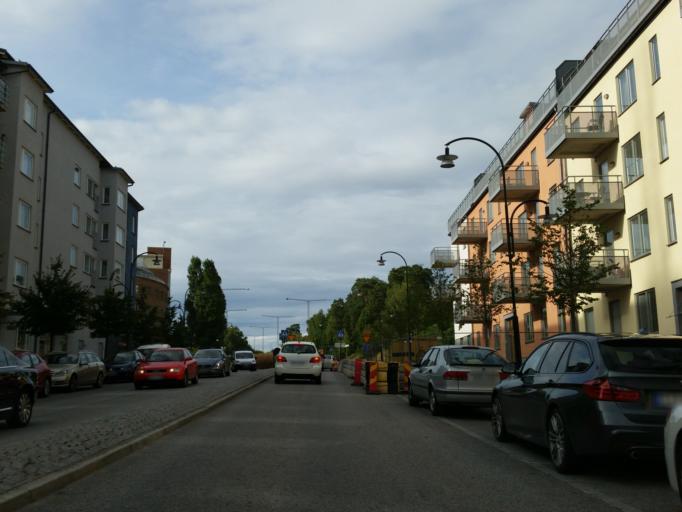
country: SE
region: Stockholm
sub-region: Sollentuna Kommun
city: Sollentuna
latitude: 59.4298
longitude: 17.9516
